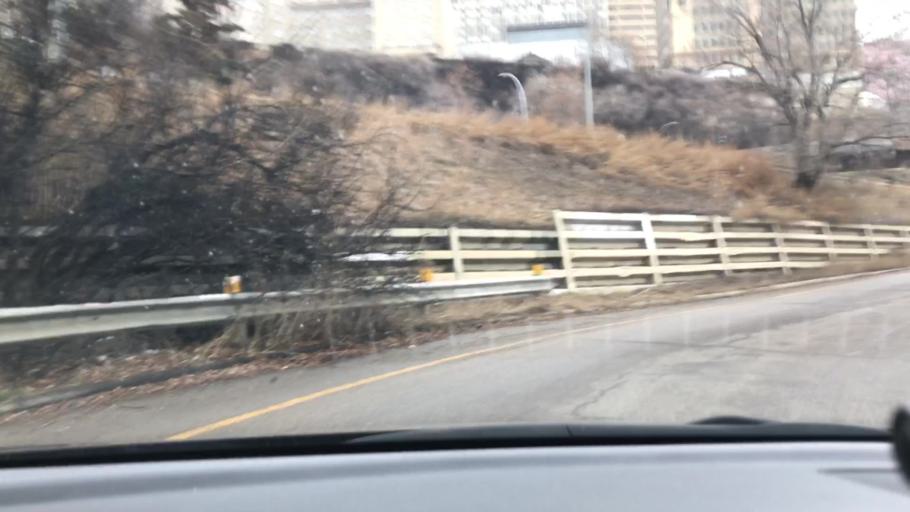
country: CA
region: Alberta
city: Edmonton
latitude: 53.5386
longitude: -113.4883
